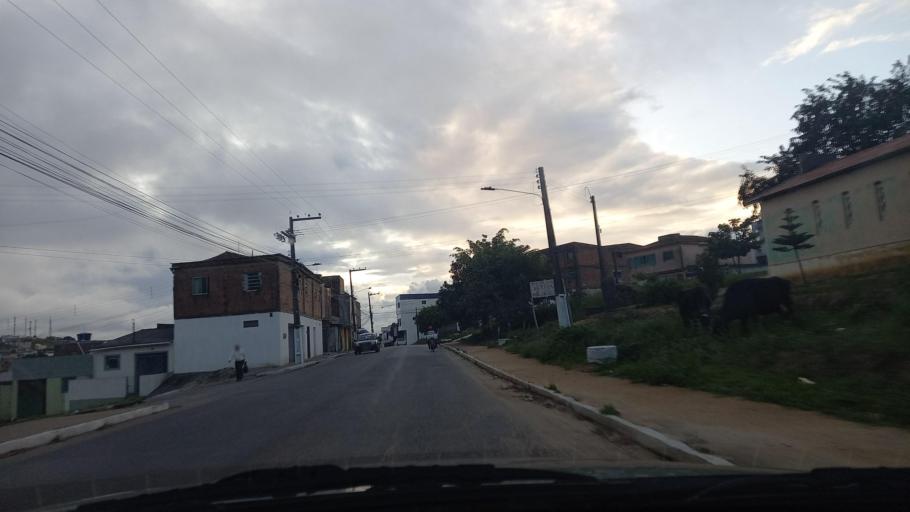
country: BR
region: Pernambuco
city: Garanhuns
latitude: -8.8889
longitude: -36.4596
